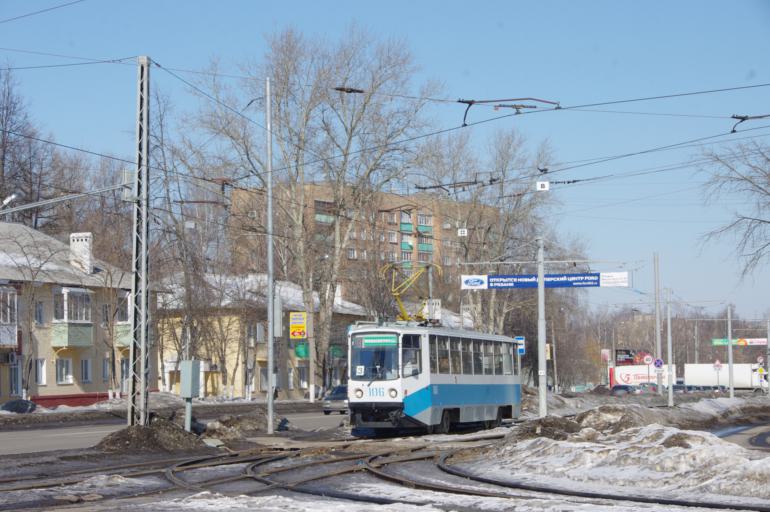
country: RU
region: Moskovskaya
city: Kolomna
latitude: 55.0805
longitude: 38.7629
